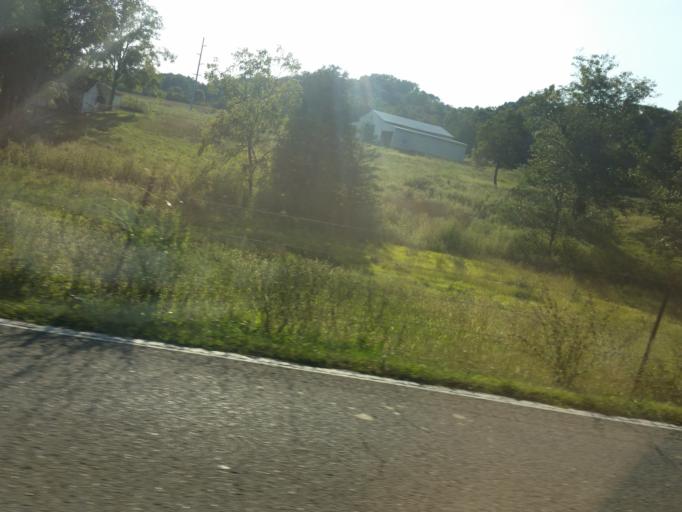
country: US
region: Tennessee
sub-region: Union County
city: Maynardville
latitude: 36.2232
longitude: -83.8373
